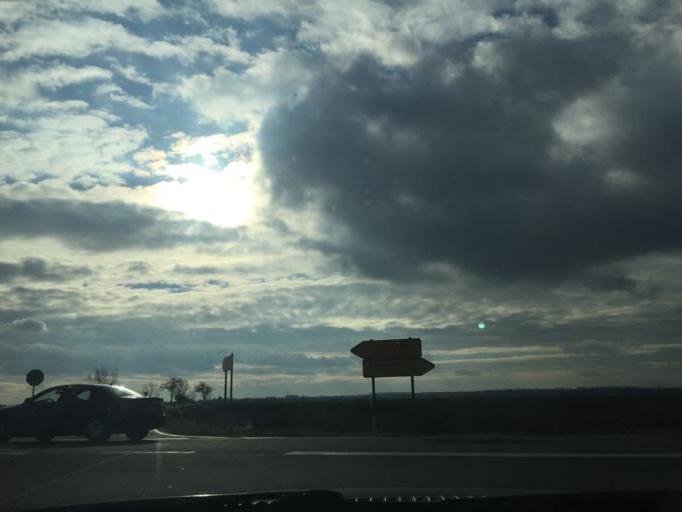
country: DE
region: Saxony
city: Ebersbach
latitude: 51.2659
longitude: 13.6661
